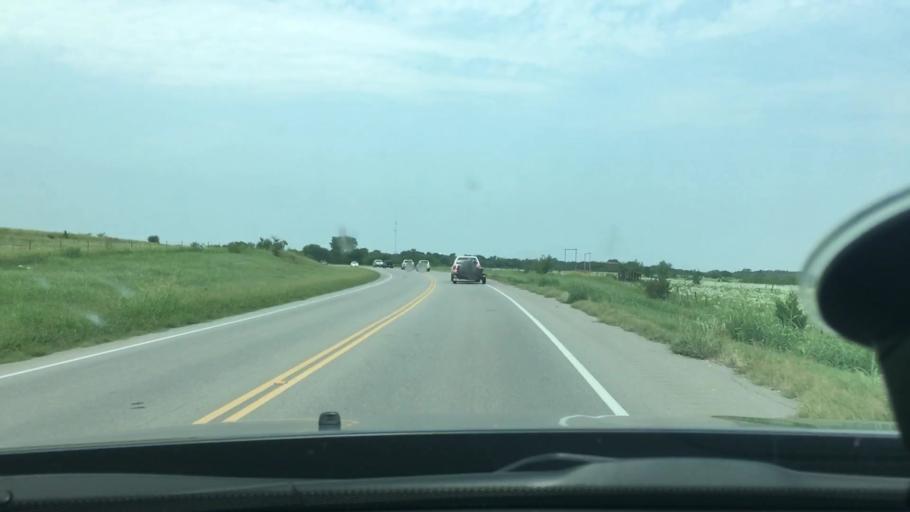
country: US
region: Oklahoma
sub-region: Marshall County
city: Madill
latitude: 34.0590
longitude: -96.7501
